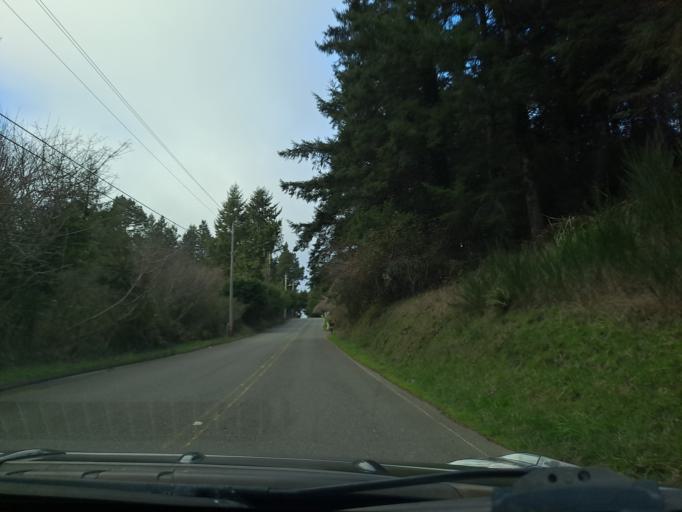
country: US
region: California
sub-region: Humboldt County
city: Fortuna
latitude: 40.6051
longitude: -124.1615
